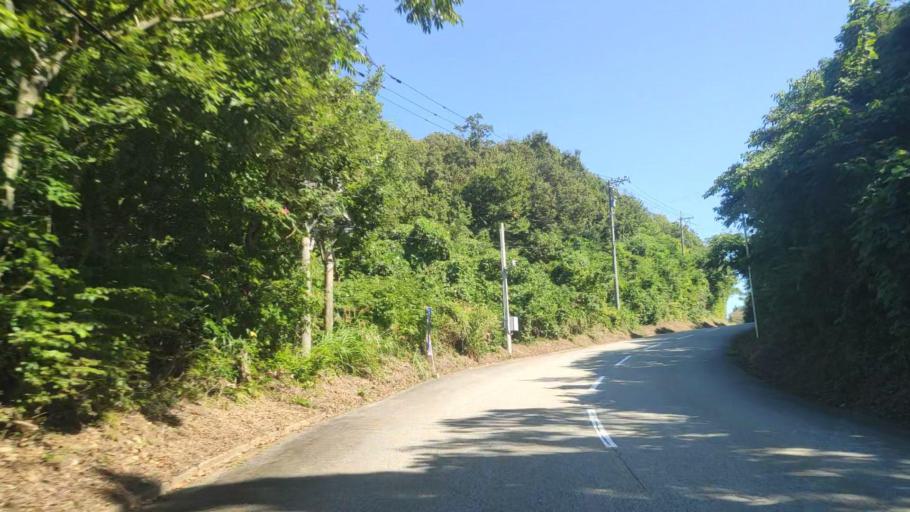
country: JP
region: Ishikawa
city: Nanao
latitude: 37.5156
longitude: 137.3317
